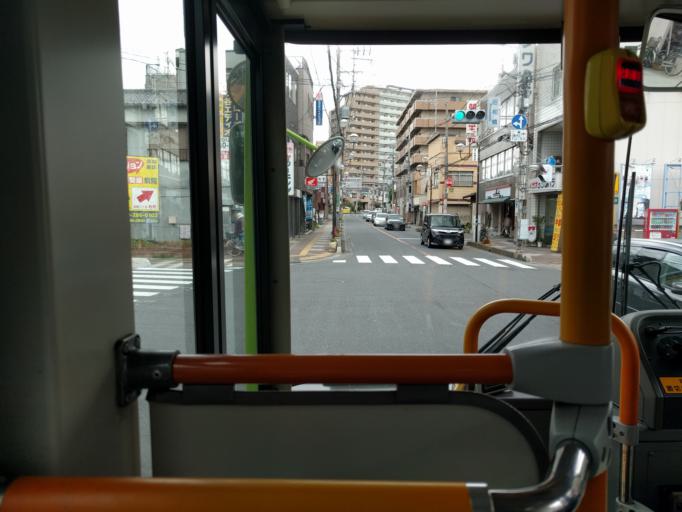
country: JP
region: Saitama
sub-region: Kawaguchi-shi
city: Hatogaya-honcho
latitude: 35.8301
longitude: 139.7393
